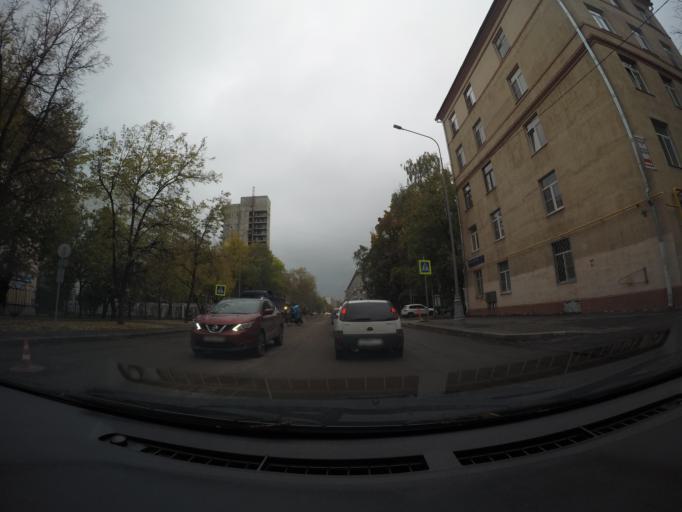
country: RU
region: Moskovskaya
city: Izmaylovo
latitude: 55.7626
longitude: 37.7924
